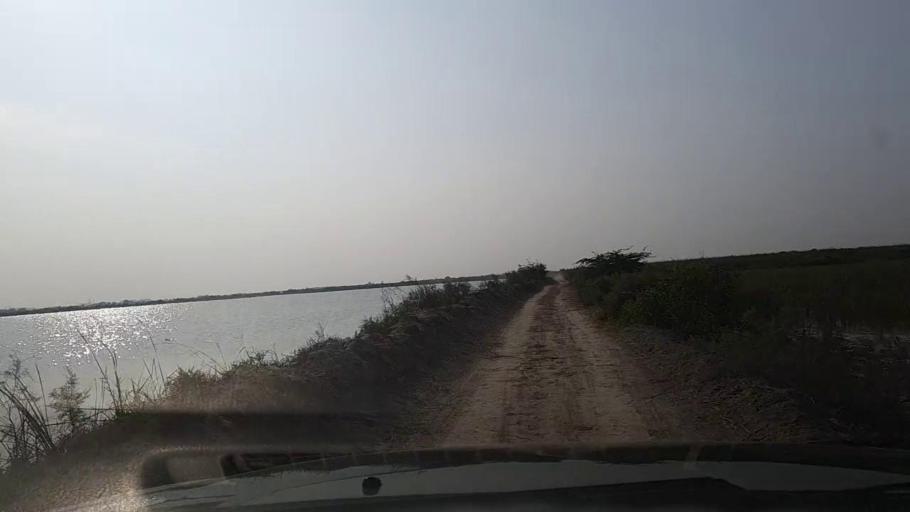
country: PK
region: Sindh
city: Mirpur Batoro
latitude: 24.6478
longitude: 68.2859
